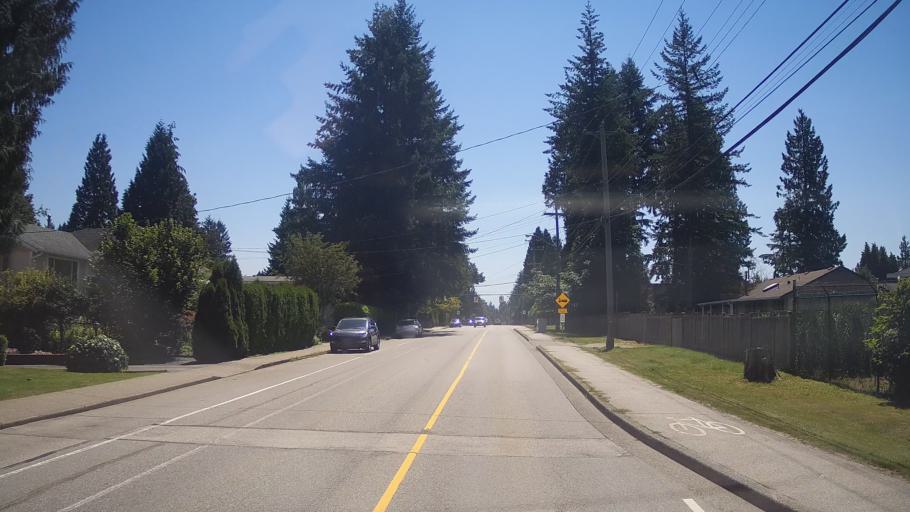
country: CA
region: British Columbia
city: Port Moody
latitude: 49.2760
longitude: -122.8808
